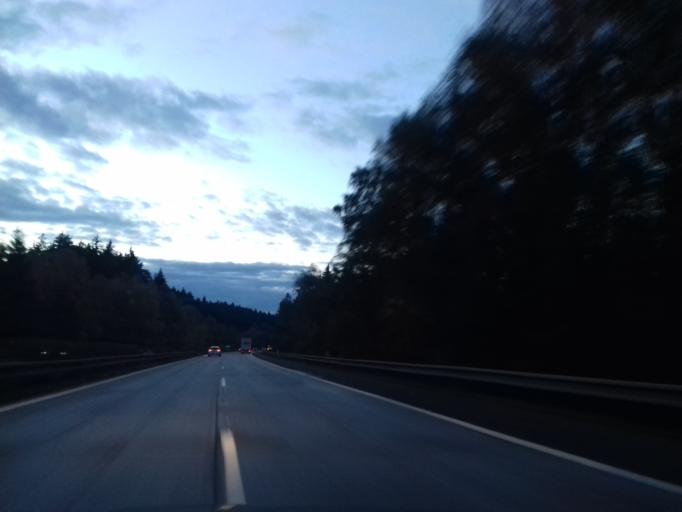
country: CZ
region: Central Bohemia
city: Divisov
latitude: 49.8092
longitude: 14.8882
